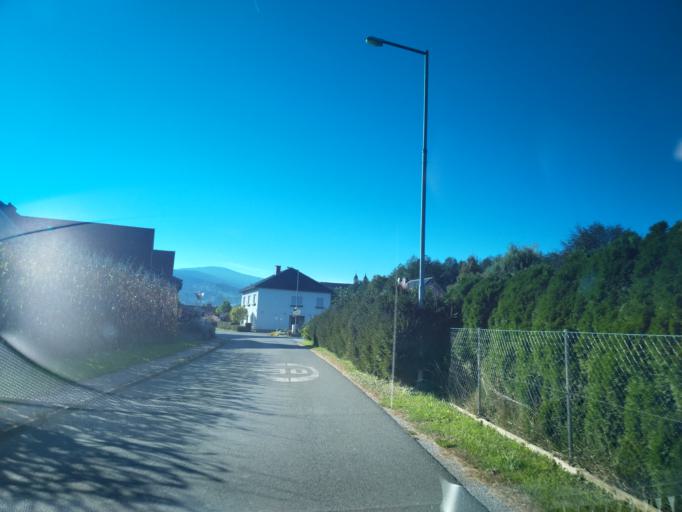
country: AT
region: Styria
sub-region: Politischer Bezirk Deutschlandsberg
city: Stainz
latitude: 46.8946
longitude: 15.2730
